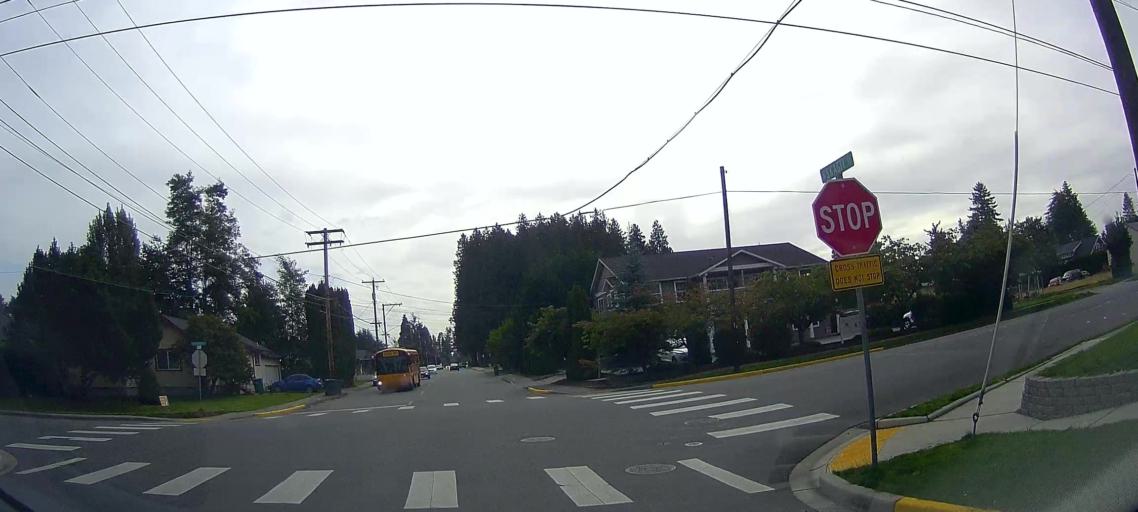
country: US
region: Washington
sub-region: Skagit County
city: Burlington
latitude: 48.4756
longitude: -122.3192
